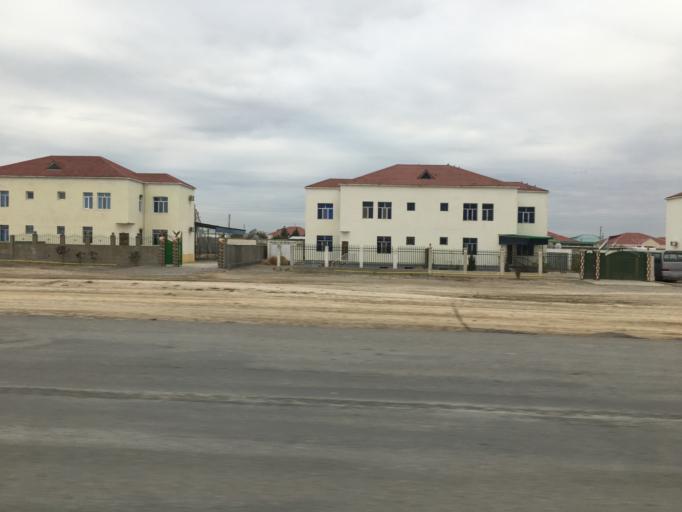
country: TM
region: Ahal
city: Kaka
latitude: 37.3580
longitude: 59.6354
